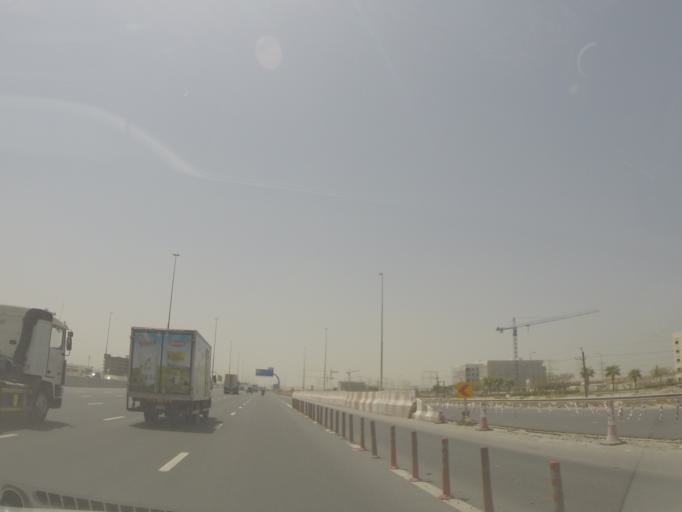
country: AE
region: Dubai
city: Dubai
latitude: 25.0362
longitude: 55.1795
